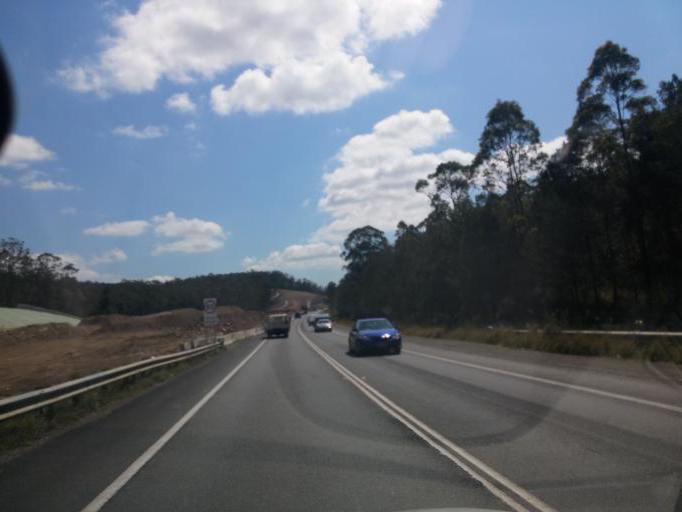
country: AU
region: New South Wales
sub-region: Port Macquarie-Hastings
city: North Shore
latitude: -31.2746
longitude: 152.8125
